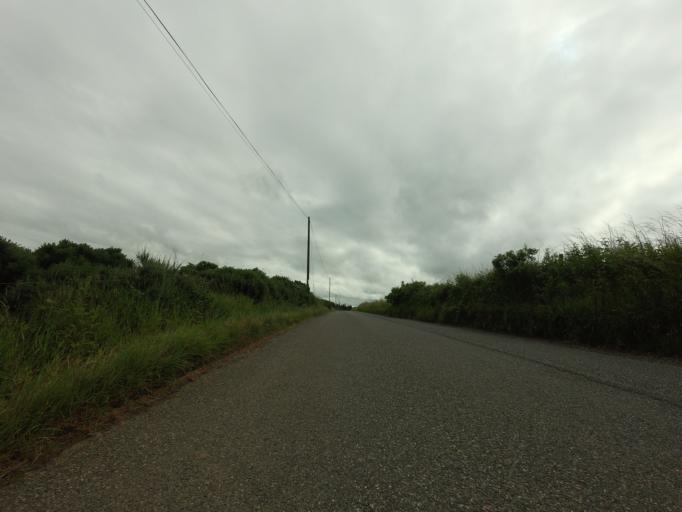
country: GB
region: Scotland
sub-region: Aberdeenshire
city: Turriff
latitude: 57.5389
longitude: -2.3708
